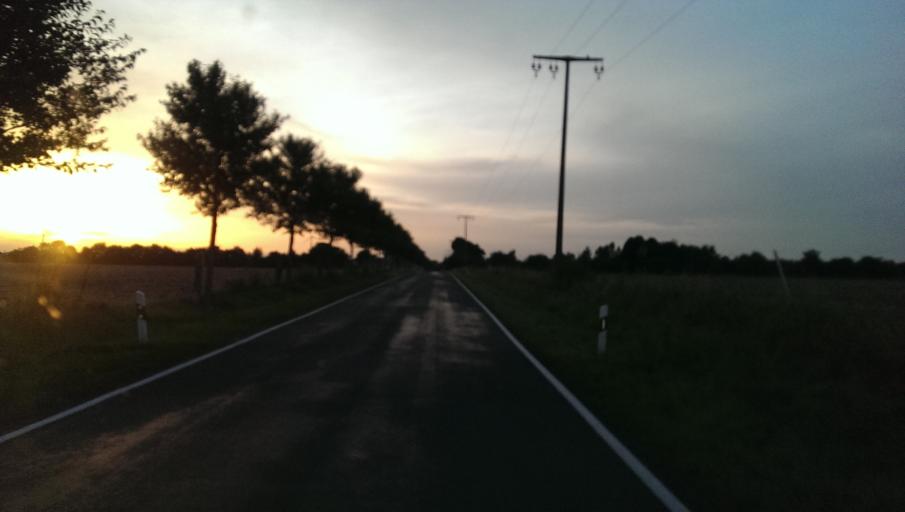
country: DE
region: Saxony-Anhalt
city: Kropstadt
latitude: 51.9962
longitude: 12.7857
